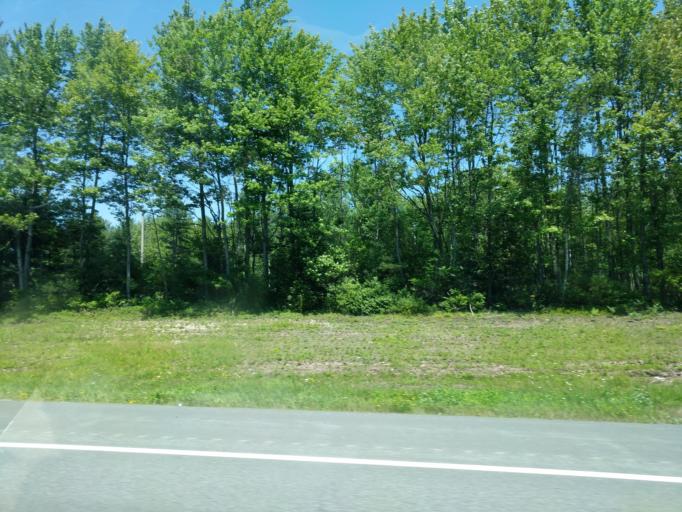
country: US
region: New York
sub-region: Sullivan County
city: Monticello
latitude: 41.6484
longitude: -74.6547
